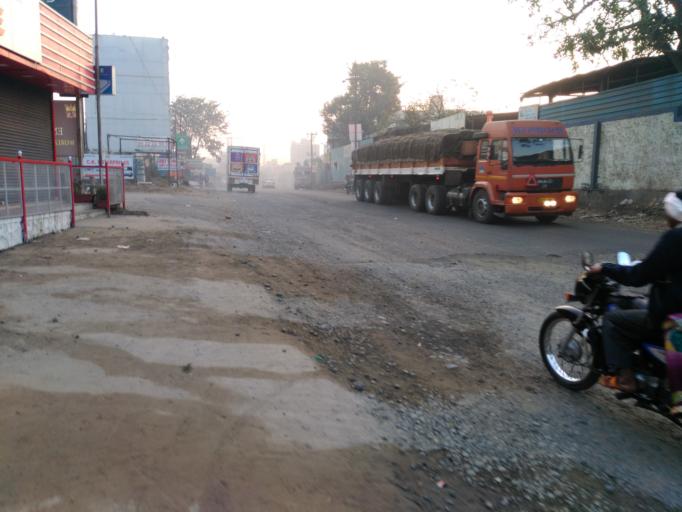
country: IN
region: Maharashtra
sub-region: Pune Division
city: Pune
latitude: 18.4491
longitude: 73.9057
